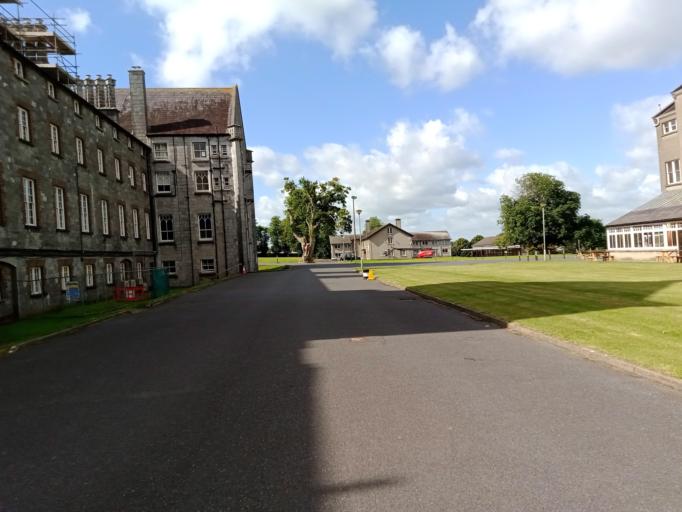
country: IE
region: Leinster
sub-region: Kilkenny
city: Kilkenny
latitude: 52.6472
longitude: -7.2553
